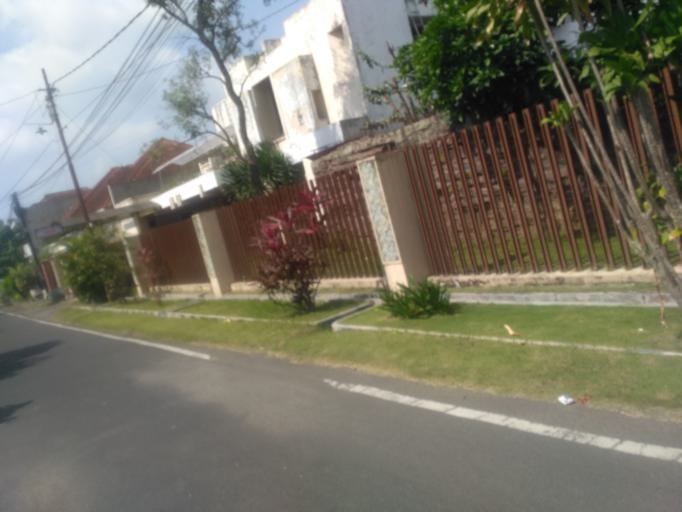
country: ID
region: East Java
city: Malang
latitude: -7.9433
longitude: 112.6357
